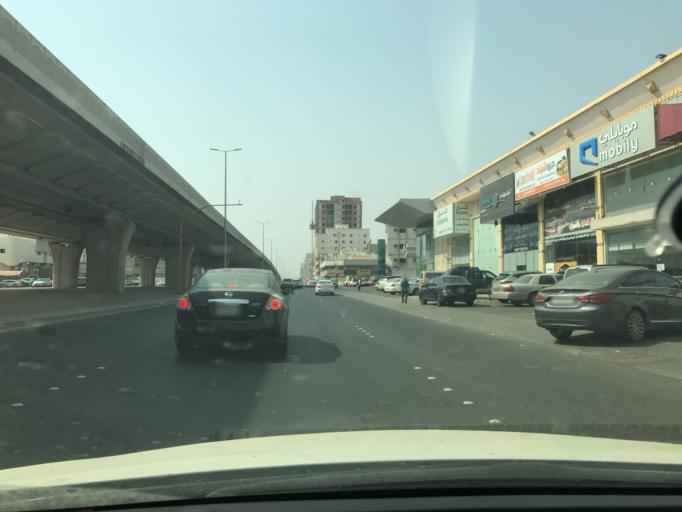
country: SA
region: Makkah
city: Jeddah
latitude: 21.6183
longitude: 39.1662
